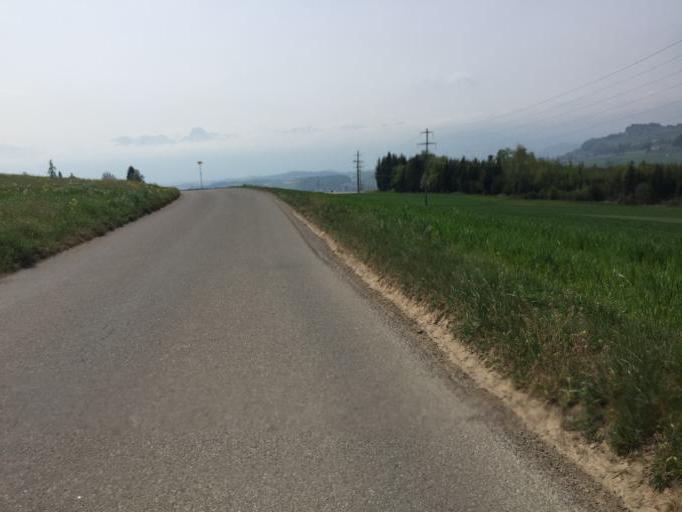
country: CH
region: Bern
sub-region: Bern-Mittelland District
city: Taegertschi
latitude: 46.8655
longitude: 7.5814
